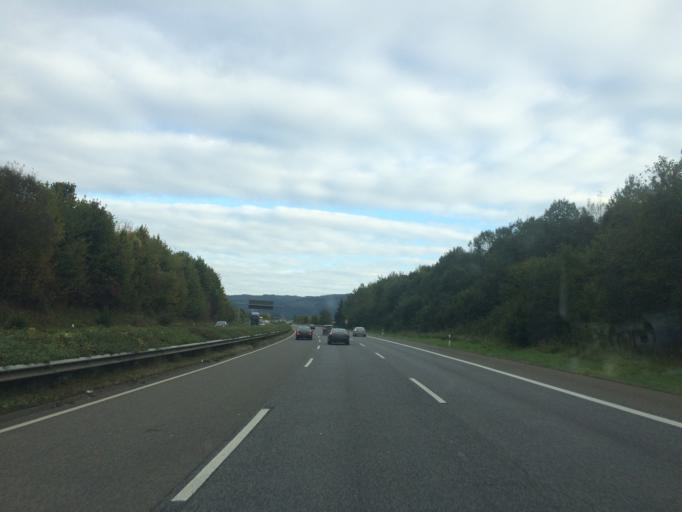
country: DE
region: Rheinland-Pfalz
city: Longuich
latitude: 49.8013
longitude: 6.7634
